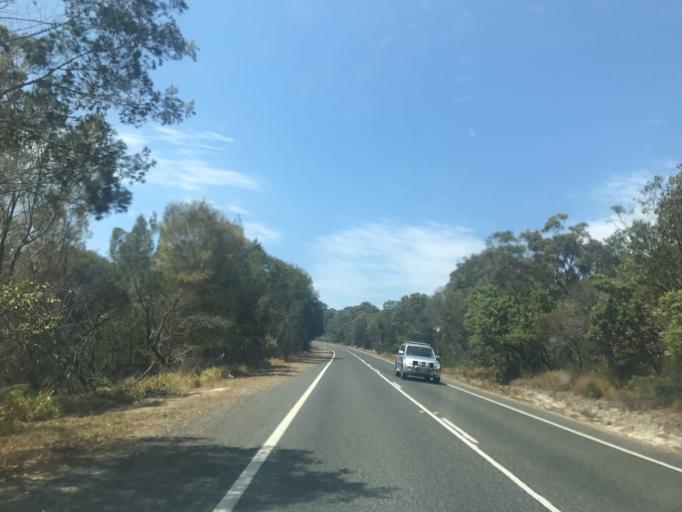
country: AU
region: Queensland
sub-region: Redland
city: Victoria Point
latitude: -27.4392
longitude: 153.4765
